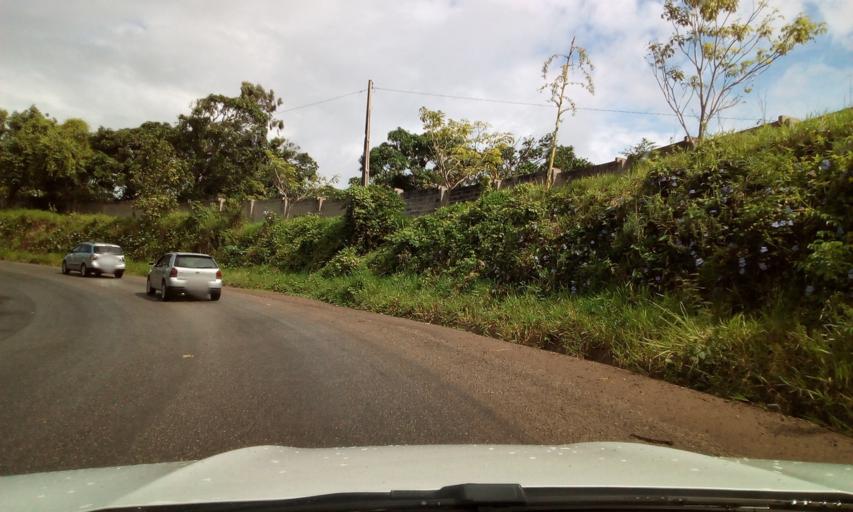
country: BR
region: Paraiba
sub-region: Areia
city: Areia
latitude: -6.9486
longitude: -35.6677
